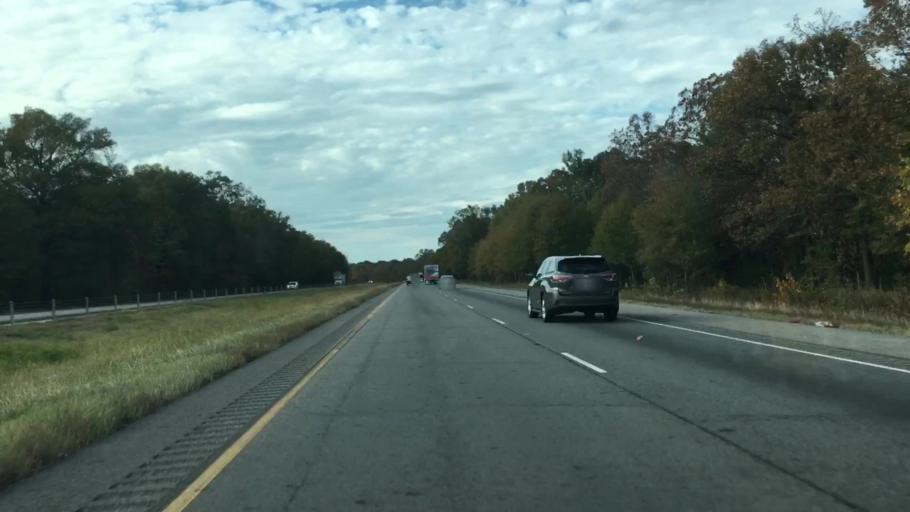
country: US
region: Arkansas
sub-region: Pope County
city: Atkins
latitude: 35.2411
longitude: -92.8590
